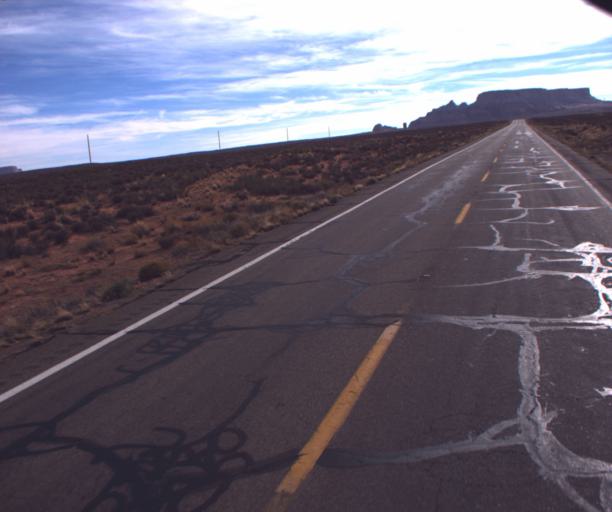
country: US
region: Arizona
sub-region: Coconino County
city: LeChee
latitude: 36.8884
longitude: -111.3652
